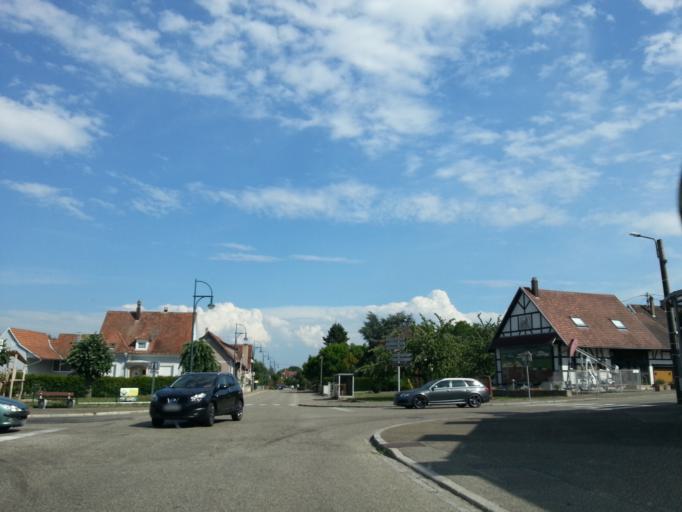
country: FR
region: Alsace
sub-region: Departement du Bas-Rhin
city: Surbourg
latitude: 48.9388
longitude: 7.8274
